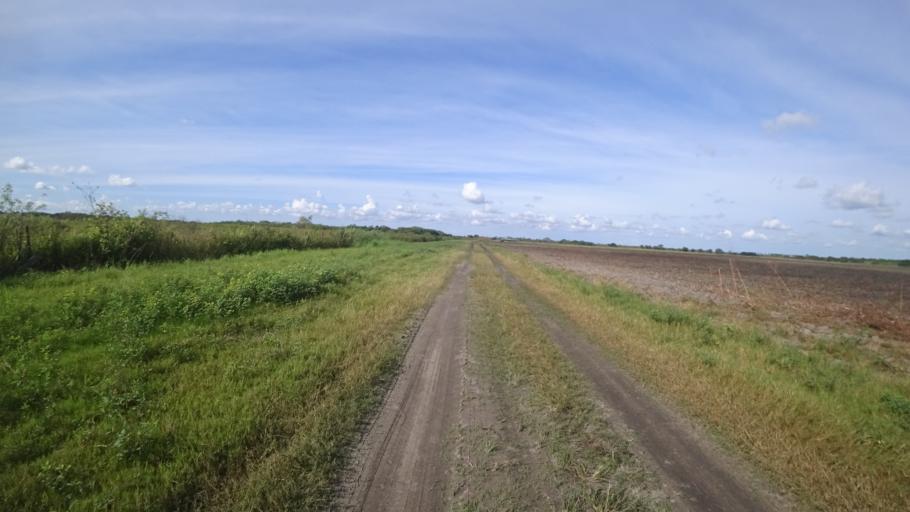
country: US
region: Florida
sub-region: Sarasota County
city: The Meadows
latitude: 27.4440
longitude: -82.3176
